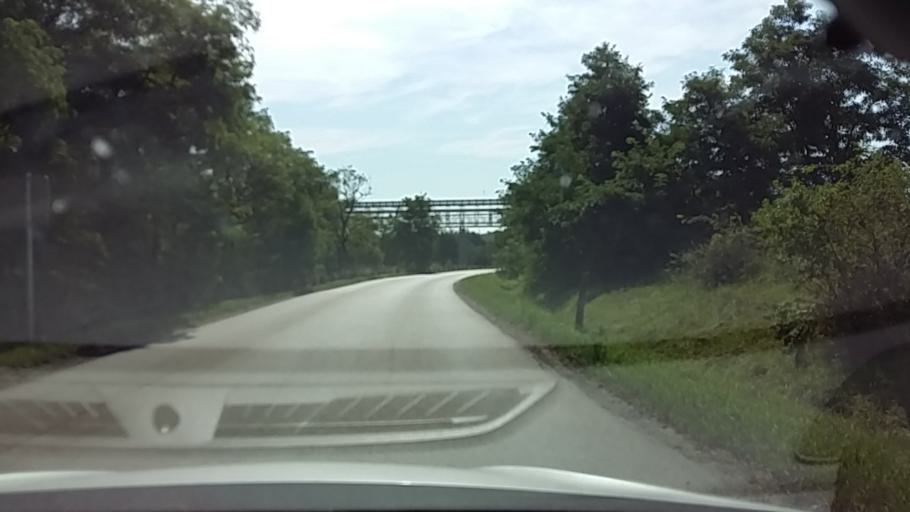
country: HU
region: Heves
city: Abasar
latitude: 47.7875
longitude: 20.0607
